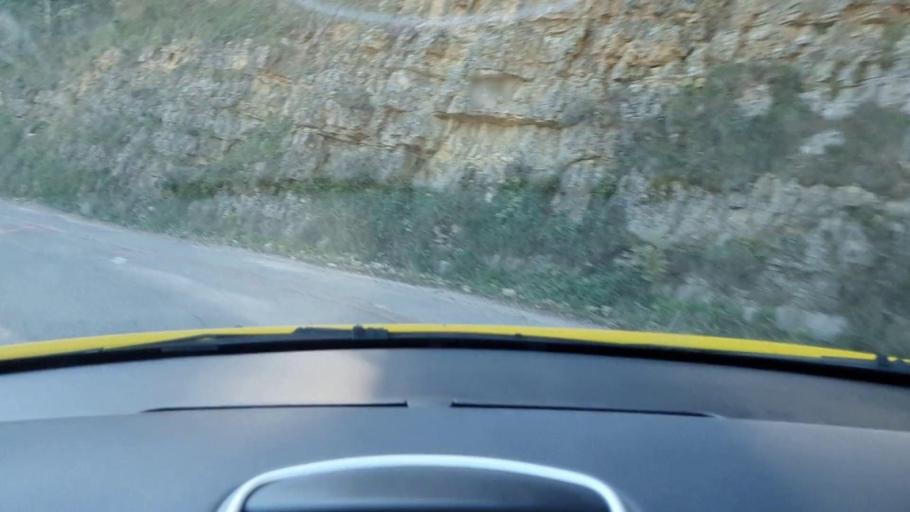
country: FR
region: Languedoc-Roussillon
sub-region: Departement du Gard
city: Aveze
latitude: 43.9629
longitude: 3.4304
